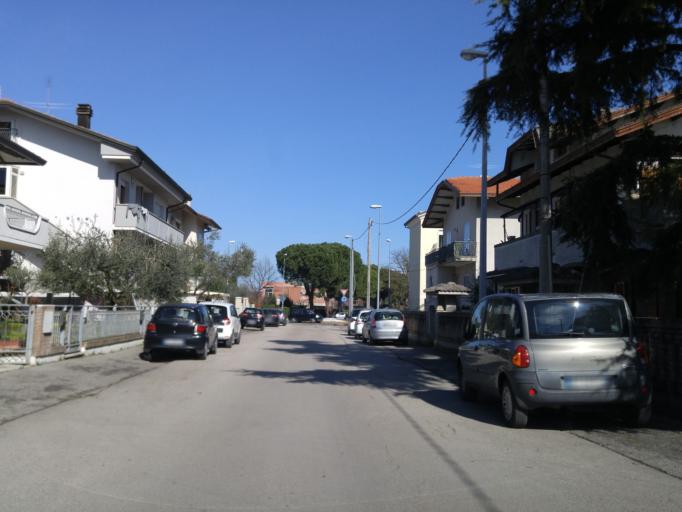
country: IT
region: Emilia-Romagna
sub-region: Provincia di Rimini
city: Cattolica
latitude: 43.9533
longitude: 12.7352
